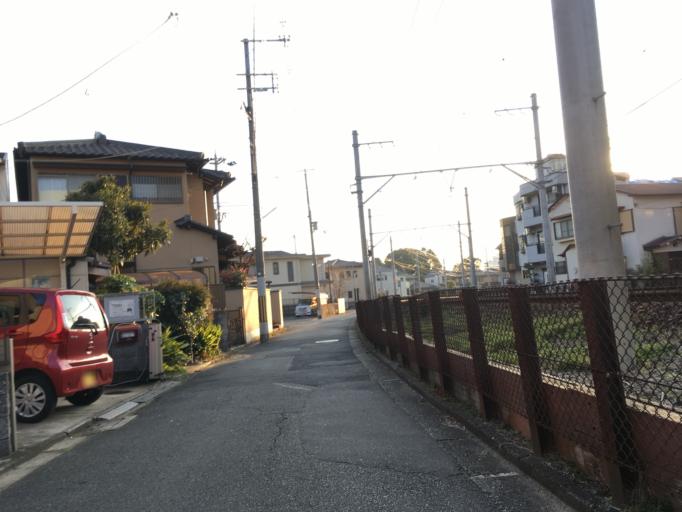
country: JP
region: Kyoto
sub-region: Kyoto-shi
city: Kamigyo-ku
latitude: 35.0362
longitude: 135.7835
